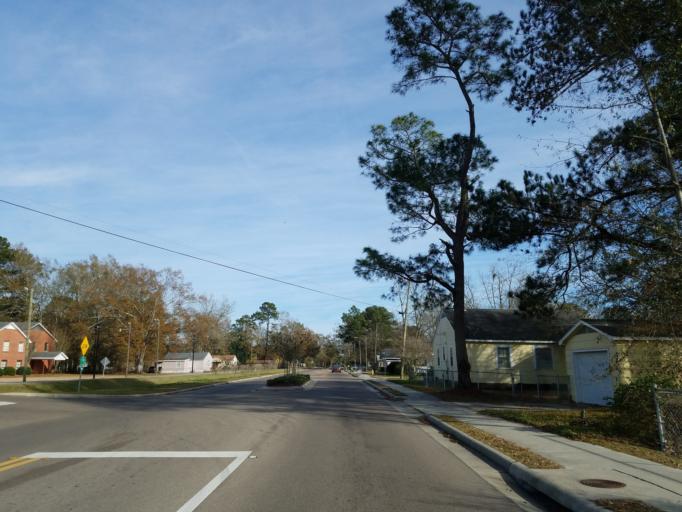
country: US
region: Mississippi
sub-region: Forrest County
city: Hattiesburg
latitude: 31.3320
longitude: -89.3197
